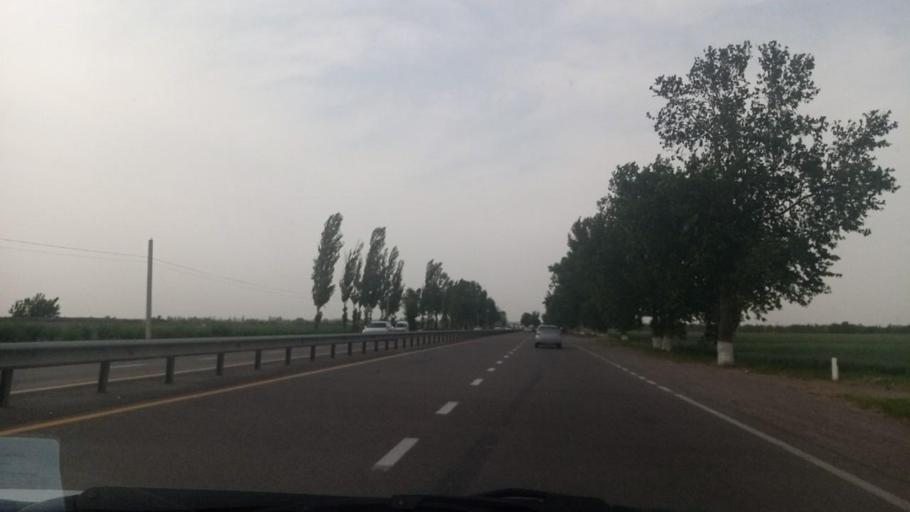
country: UZ
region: Toshkent Shahri
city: Bektemir
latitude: 41.1379
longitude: 69.4341
